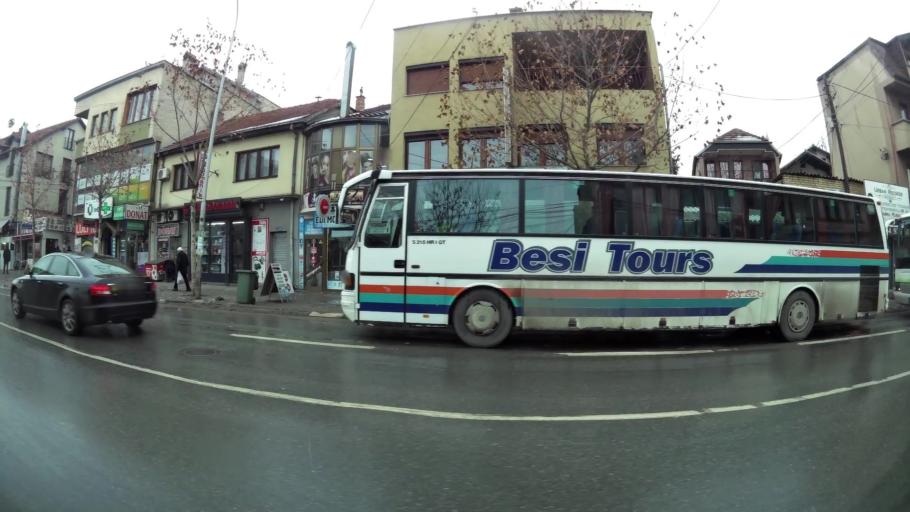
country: XK
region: Pristina
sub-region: Komuna e Prishtines
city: Pristina
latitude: 42.6699
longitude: 21.1630
